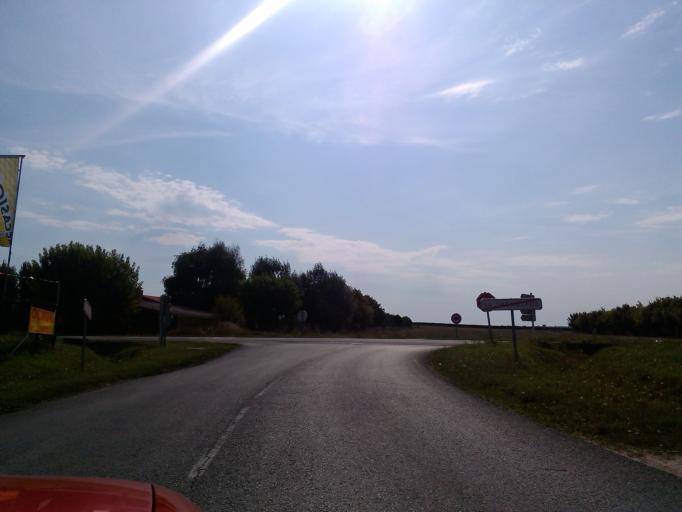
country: FR
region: Poitou-Charentes
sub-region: Departement de la Charente-Maritime
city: Arvert
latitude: 45.7593
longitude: -1.1244
